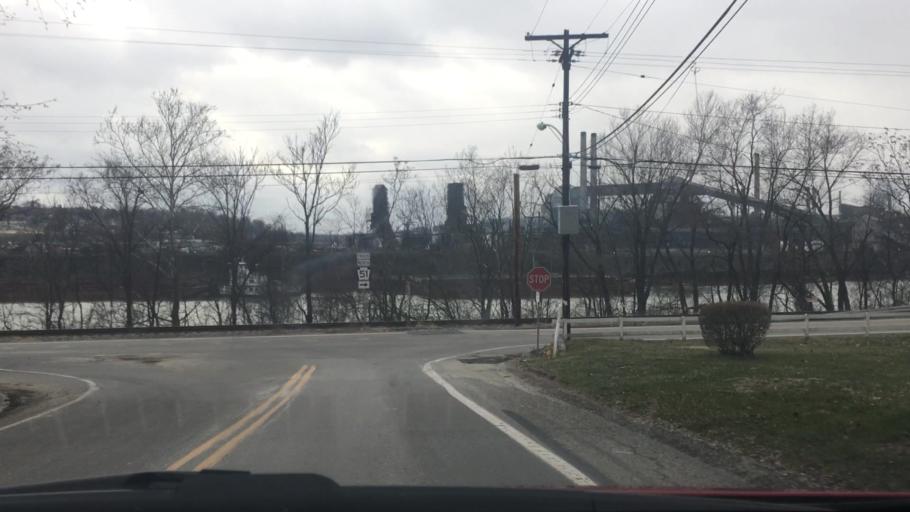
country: US
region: Pennsylvania
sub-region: Allegheny County
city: Clairton
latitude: 40.3009
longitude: -79.8656
